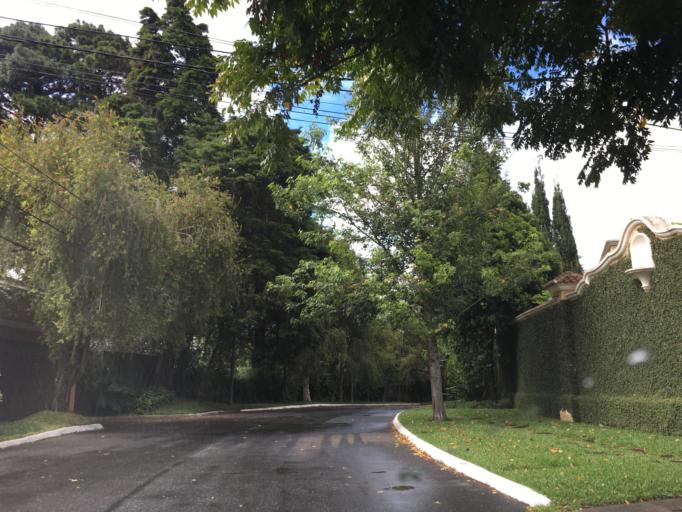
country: GT
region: Guatemala
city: Santa Catarina Pinula
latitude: 14.5827
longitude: -90.4899
